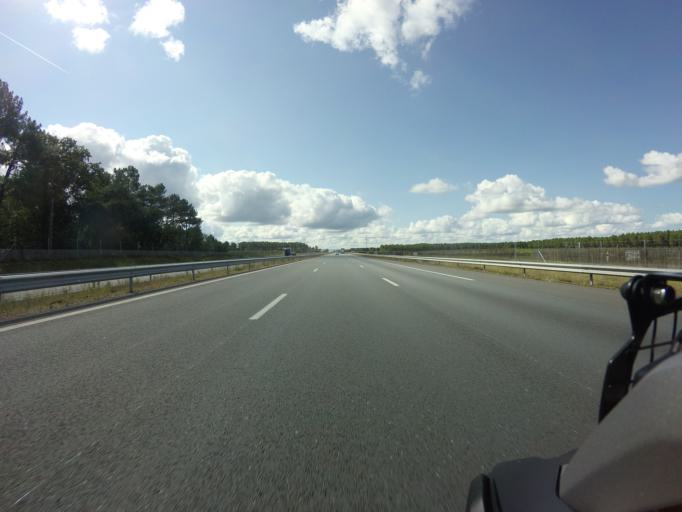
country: FR
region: Aquitaine
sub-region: Departement des Landes
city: Onesse-Laharie
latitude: 43.9971
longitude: -1.0356
